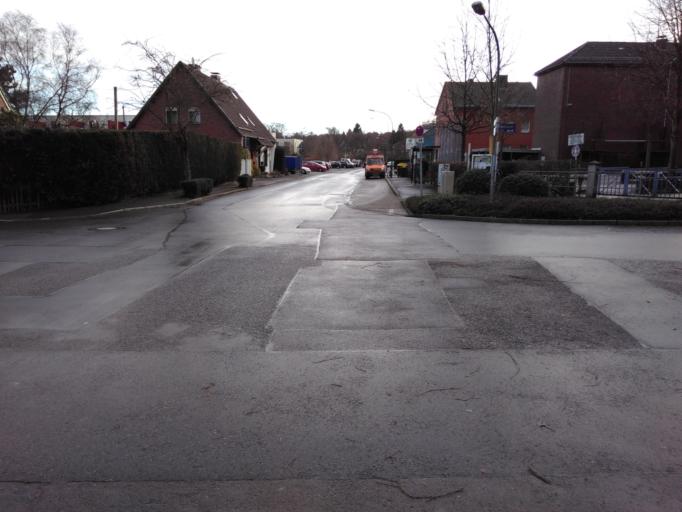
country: NL
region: Limburg
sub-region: Gemeente Vaals
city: Vaals
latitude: 50.7690
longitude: 6.0279
